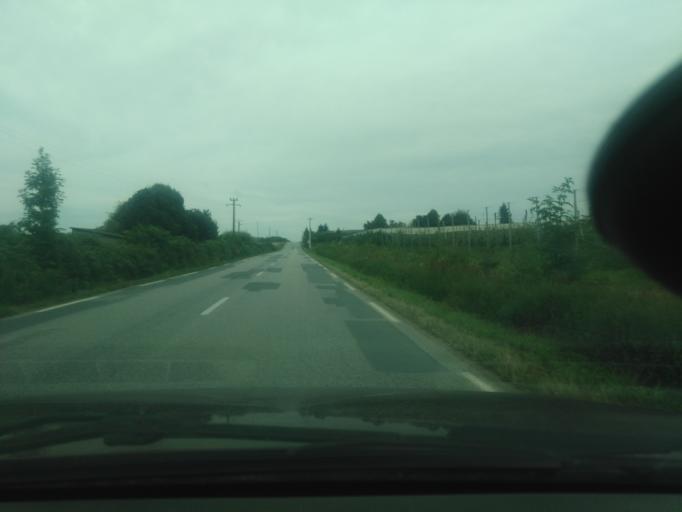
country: FR
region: Poitou-Charentes
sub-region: Departement des Deux-Sevres
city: Moncoutant
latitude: 46.6335
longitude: -0.5377
